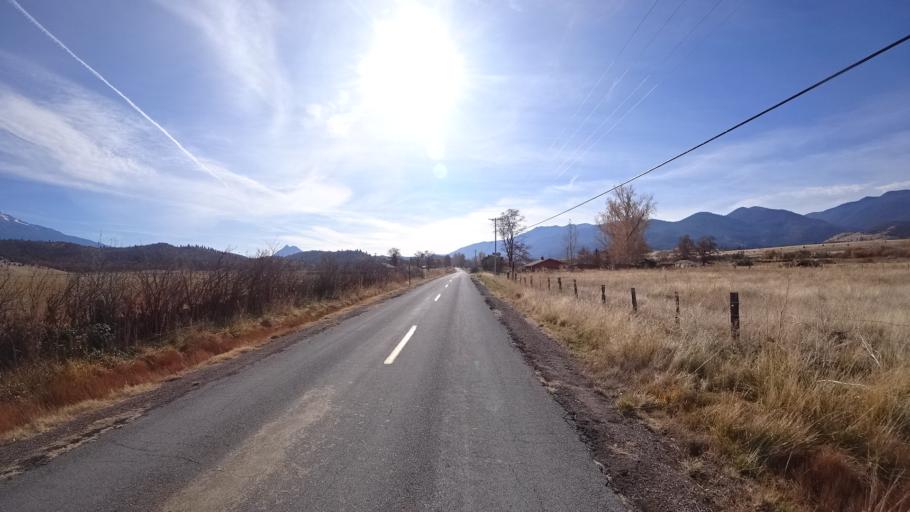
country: US
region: California
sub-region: Siskiyou County
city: Weed
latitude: 41.4667
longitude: -122.4345
